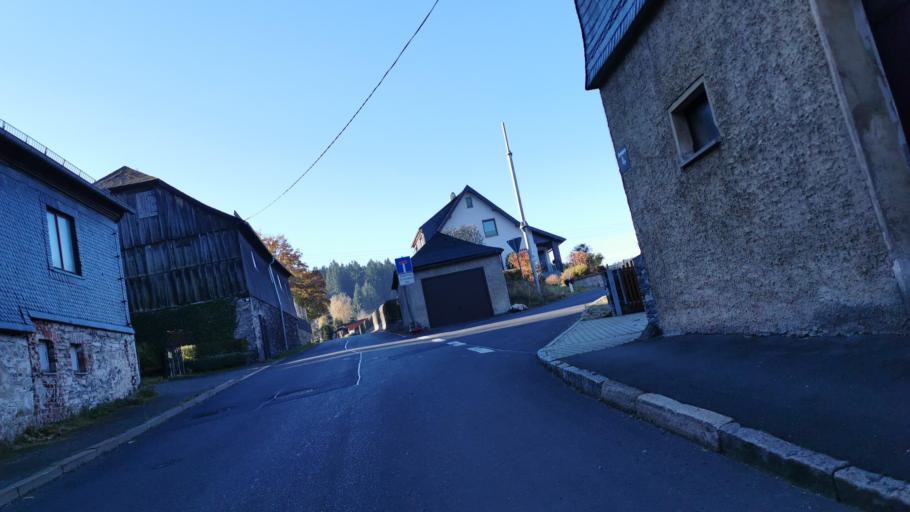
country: DE
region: Thuringia
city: Wurzbach
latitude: 50.4557
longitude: 11.5332
